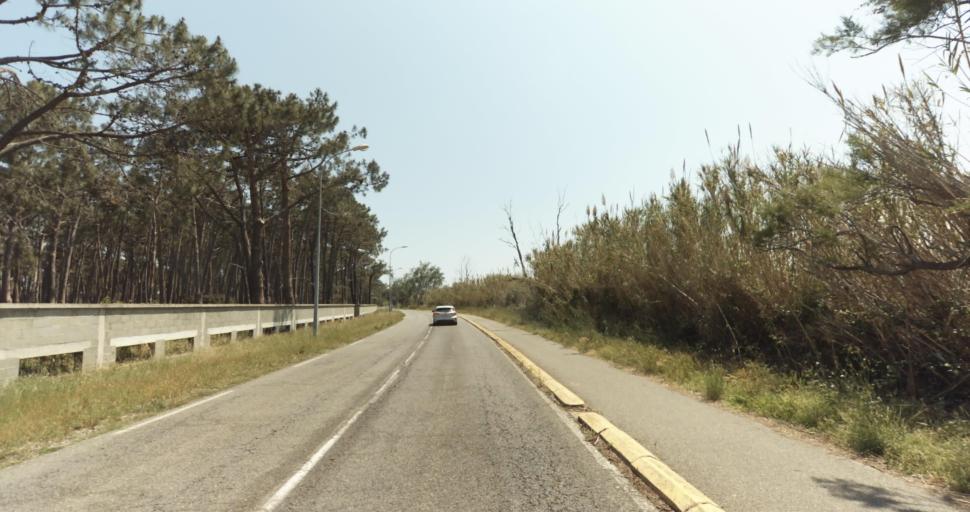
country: FR
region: Corsica
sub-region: Departement de la Haute-Corse
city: Biguglia
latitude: 42.6212
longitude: 9.4740
